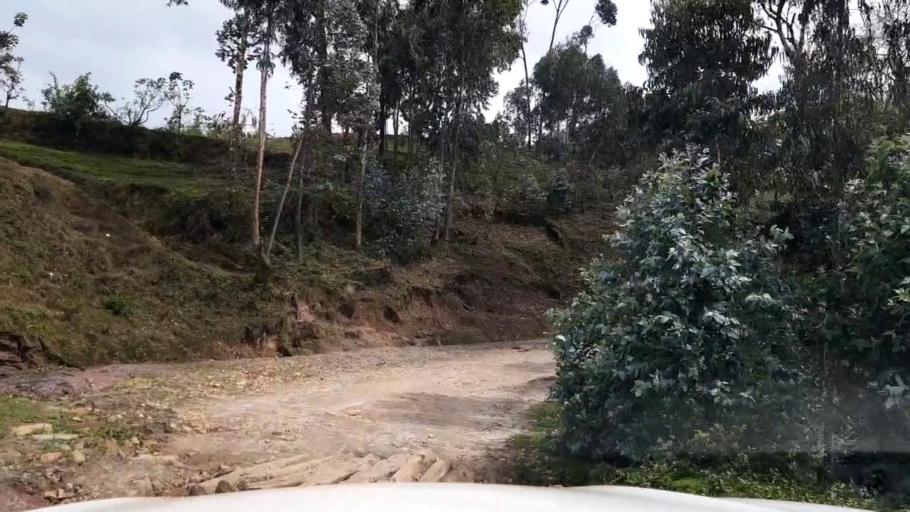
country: RW
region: Western Province
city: Kibuye
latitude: -1.9646
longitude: 29.4853
